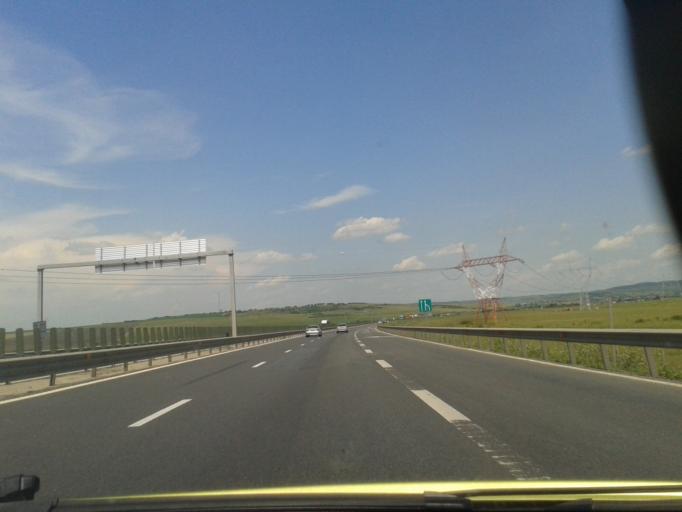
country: RO
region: Sibiu
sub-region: Comuna Sura Mica
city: Sura Mica
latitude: 45.8218
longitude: 24.0779
